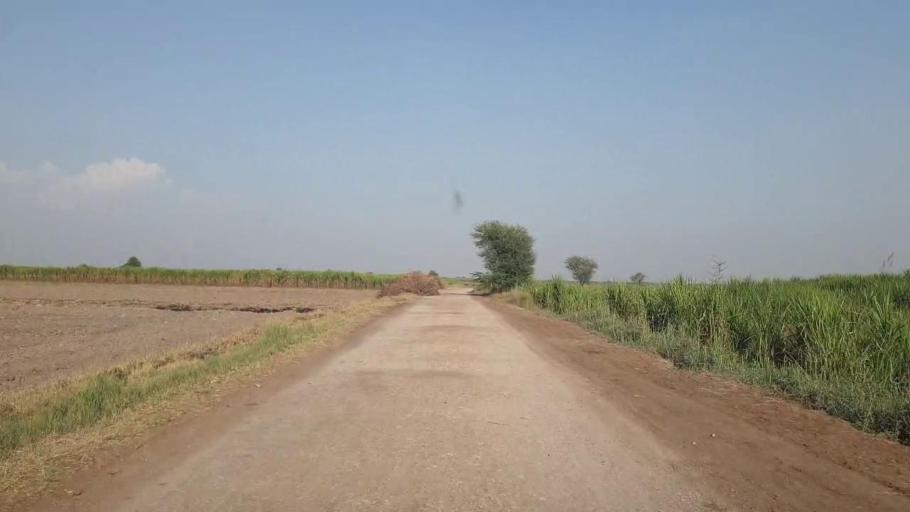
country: PK
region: Sindh
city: Sanghar
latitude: 26.0576
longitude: 68.8922
